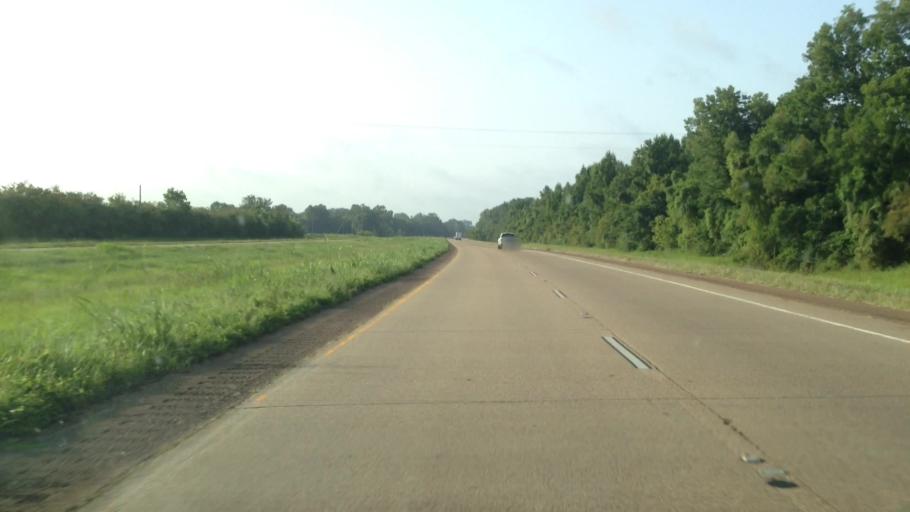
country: US
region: Louisiana
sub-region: Rapides Parish
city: Woodworth
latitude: 31.1387
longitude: -92.4503
